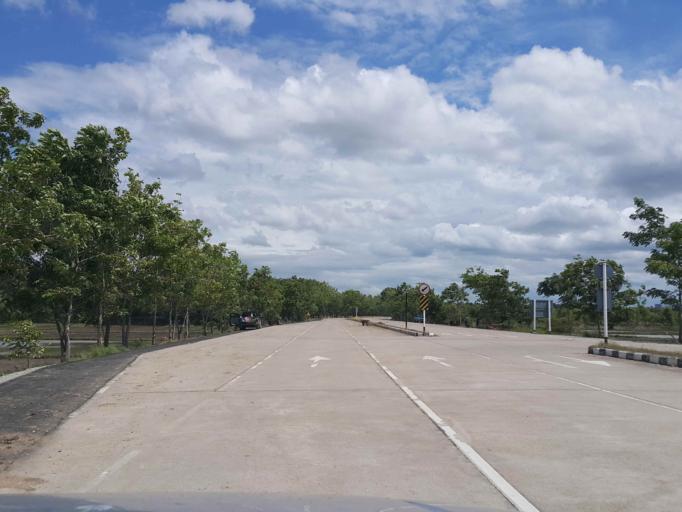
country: TH
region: Tak
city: Tak
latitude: 16.8728
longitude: 99.1126
